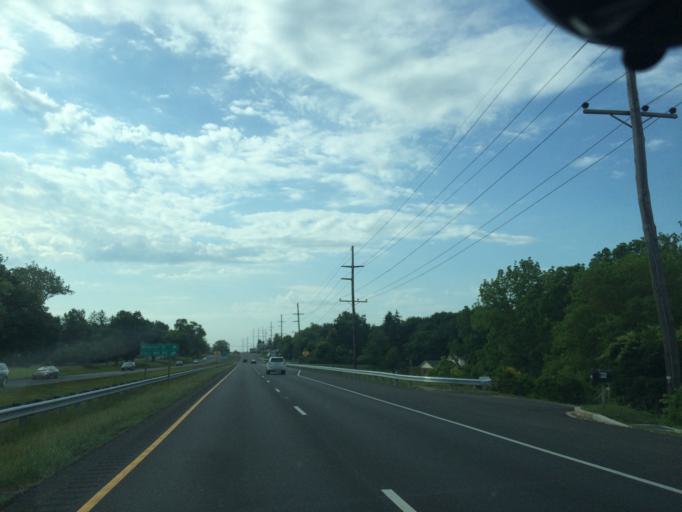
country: US
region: Maryland
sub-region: Baltimore County
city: Reisterstown
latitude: 39.5037
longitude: -76.8999
